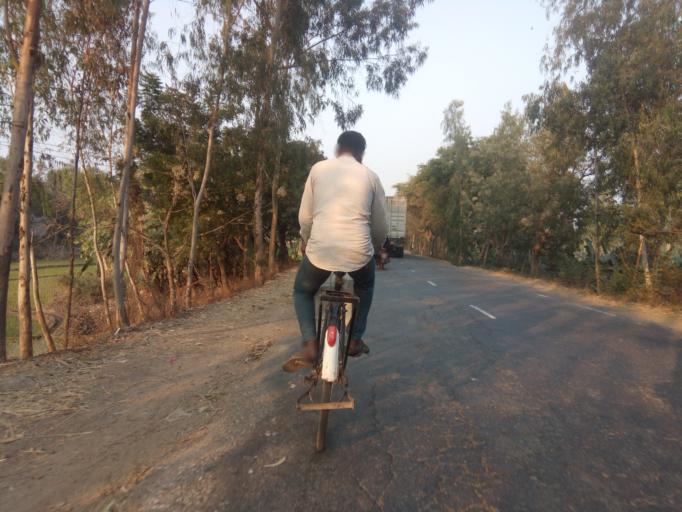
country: BD
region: Rajshahi
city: Par Naogaon
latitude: 24.5415
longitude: 89.1850
